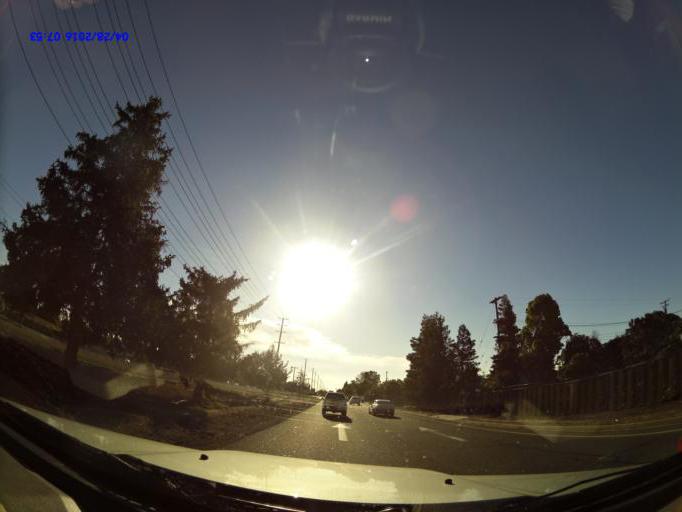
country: US
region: California
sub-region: Stanislaus County
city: Modesto
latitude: 37.6670
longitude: -120.9696
